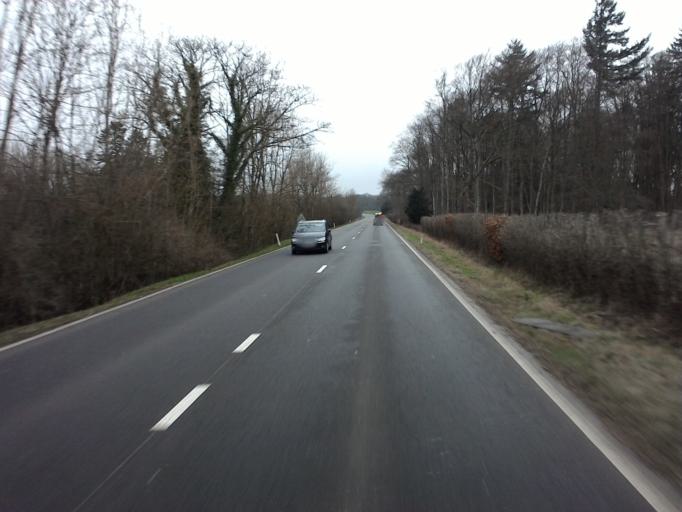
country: BE
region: Wallonia
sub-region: Province de Namur
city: Beauraing
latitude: 50.0545
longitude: 4.9803
